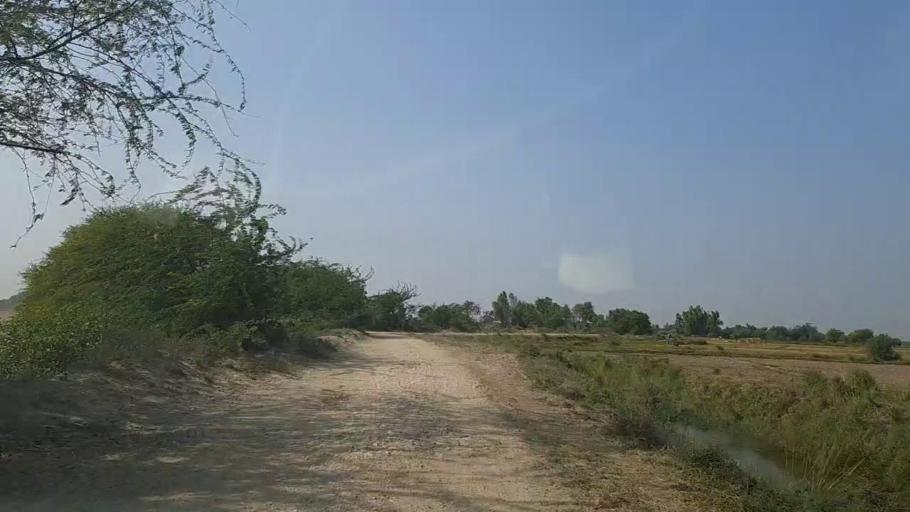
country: PK
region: Sindh
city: Mirpur Sakro
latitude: 24.5643
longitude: 67.8282
